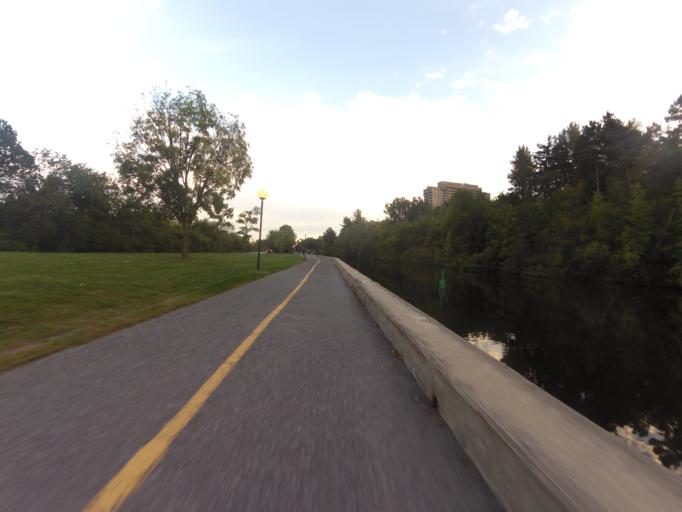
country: CA
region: Ontario
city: Ottawa
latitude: 45.3744
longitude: -75.7018
